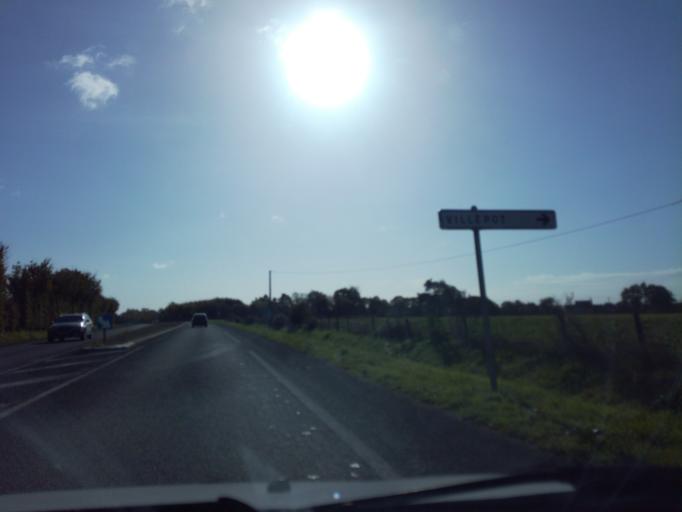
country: FR
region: Pays de la Loire
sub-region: Departement de la Loire-Atlantique
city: Soudan
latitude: 47.7776
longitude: -1.2427
